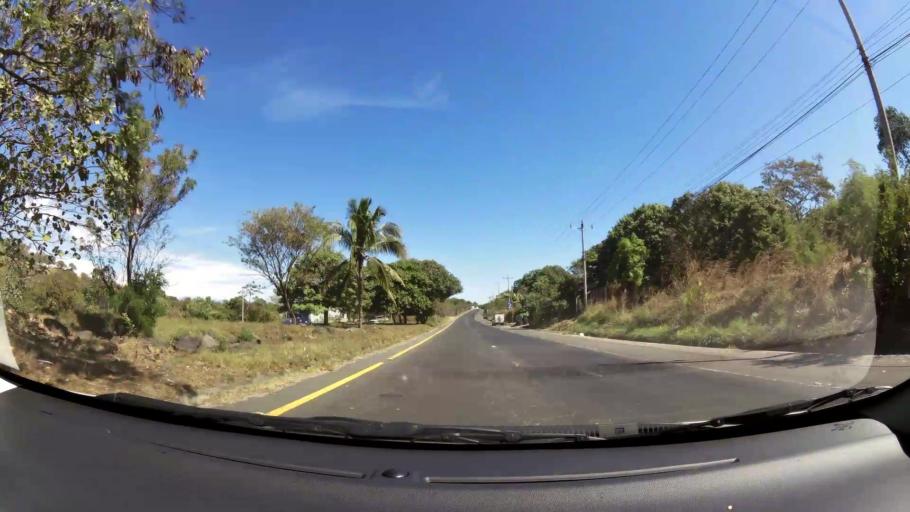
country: SV
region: La Libertad
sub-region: Distrito de Quezaltepeque
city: Quezaltepeque
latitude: 13.8097
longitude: -89.3211
